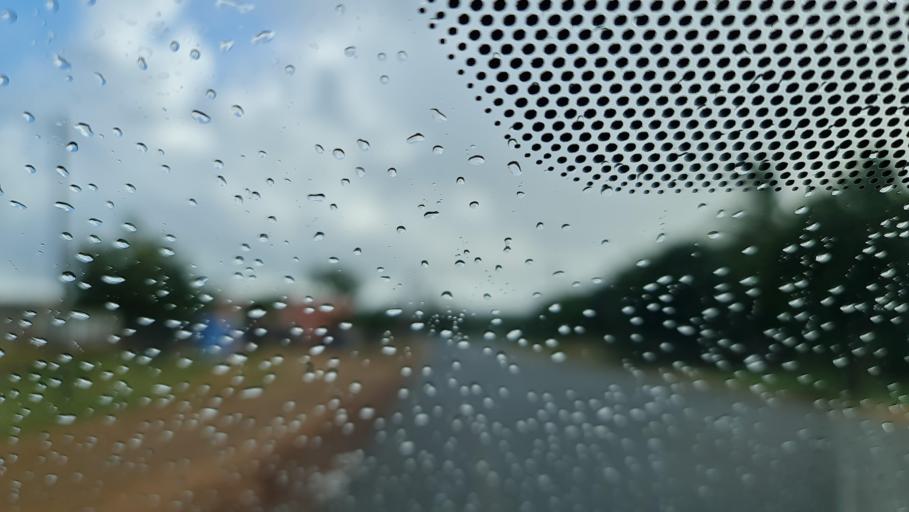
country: MZ
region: Gaza
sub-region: Xai-Xai District
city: Xai-Xai
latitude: -25.0330
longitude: 33.7239
